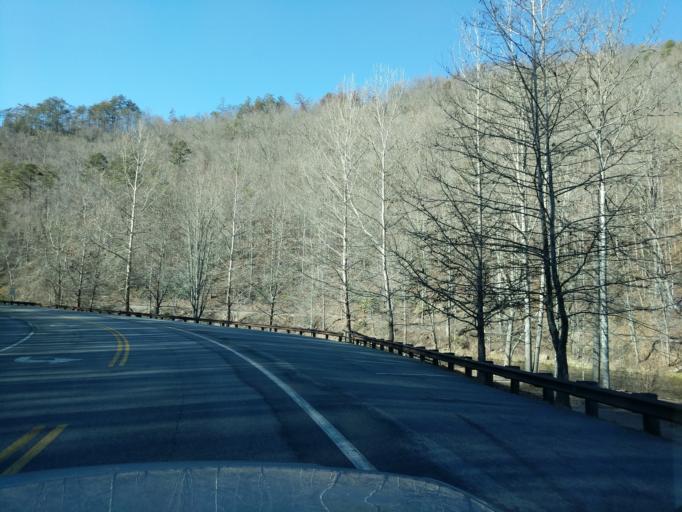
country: US
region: North Carolina
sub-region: Swain County
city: Bryson City
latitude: 35.3330
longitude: -83.5964
